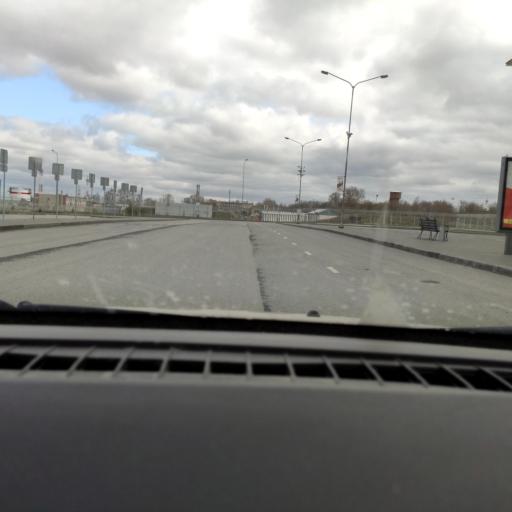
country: RU
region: Perm
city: Kultayevo
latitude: 57.9163
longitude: 56.0097
